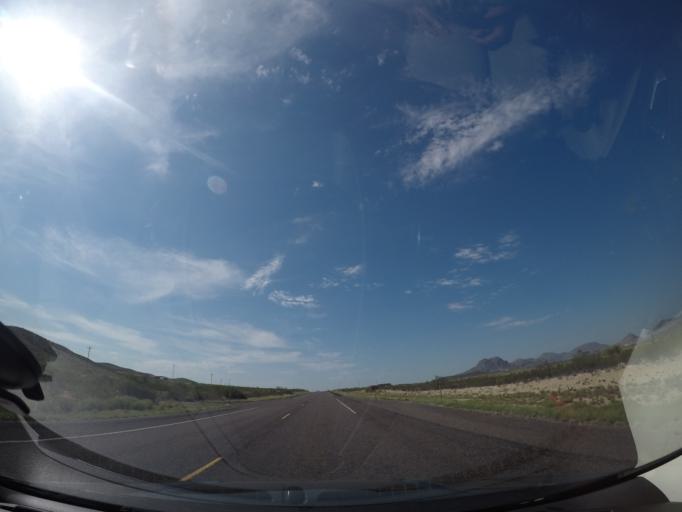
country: US
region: Texas
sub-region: Brewster County
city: Alpine
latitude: 29.5644
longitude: -103.5505
